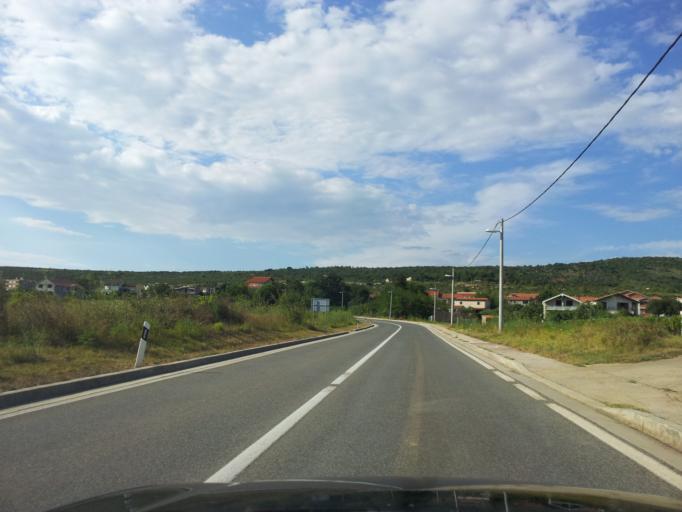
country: HR
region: Zadarska
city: Posedarje
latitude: 44.2134
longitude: 15.4686
